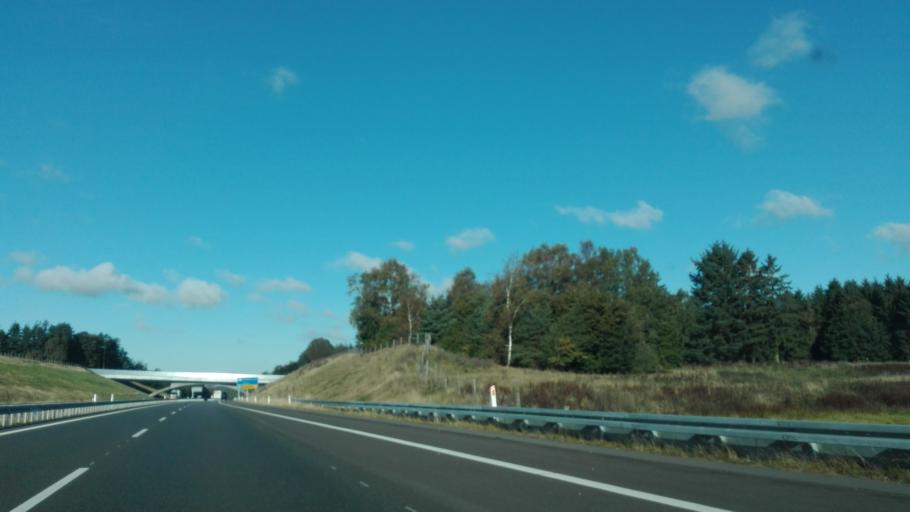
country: DK
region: Central Jutland
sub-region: Silkeborg Kommune
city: Svejbaek
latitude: 56.1552
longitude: 9.6276
